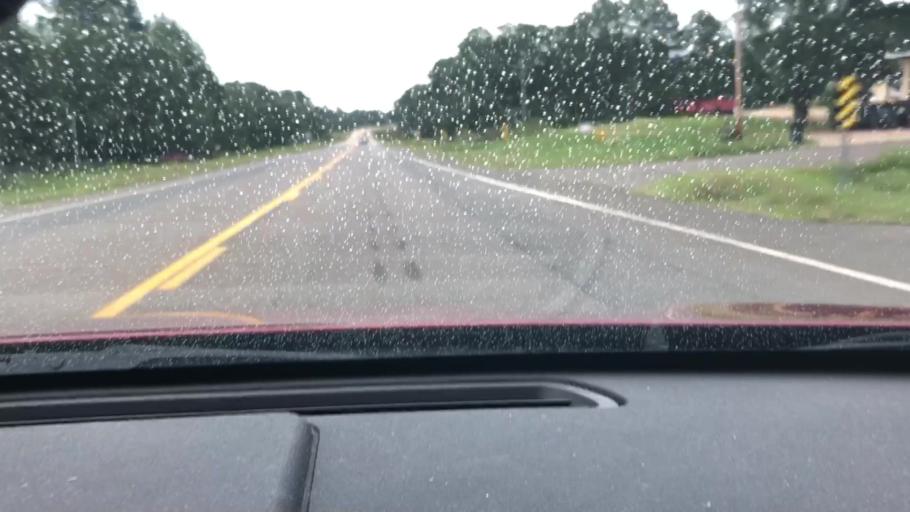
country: US
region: Arkansas
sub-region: Lafayette County
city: Lewisville
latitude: 33.3603
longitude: -93.5547
